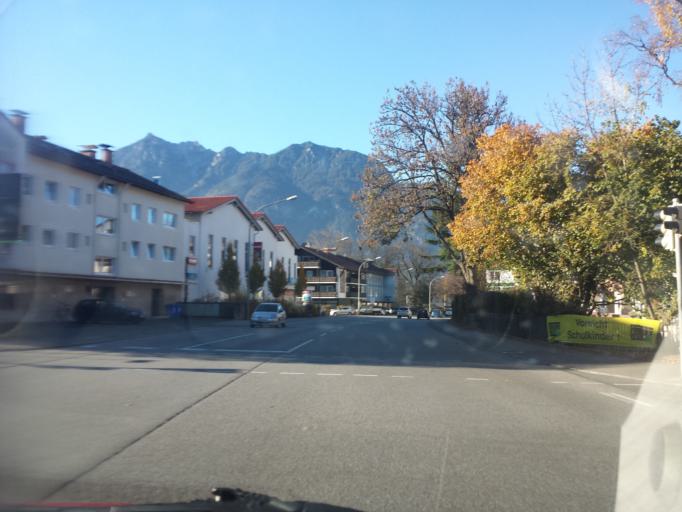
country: DE
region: Bavaria
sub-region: Upper Bavaria
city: Garmisch-Partenkirchen
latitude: 47.4915
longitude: 11.1084
